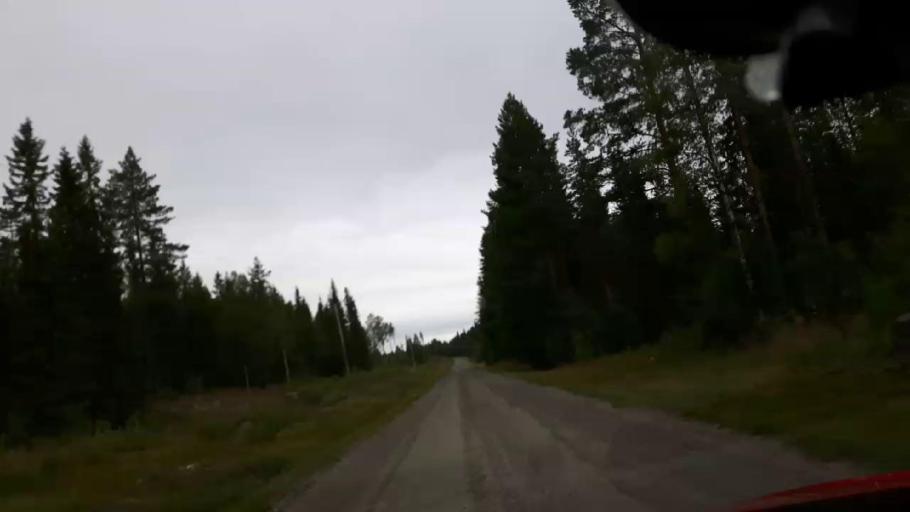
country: SE
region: Vaesternorrland
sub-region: Ange Kommun
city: Ange
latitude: 62.8544
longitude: 15.9179
